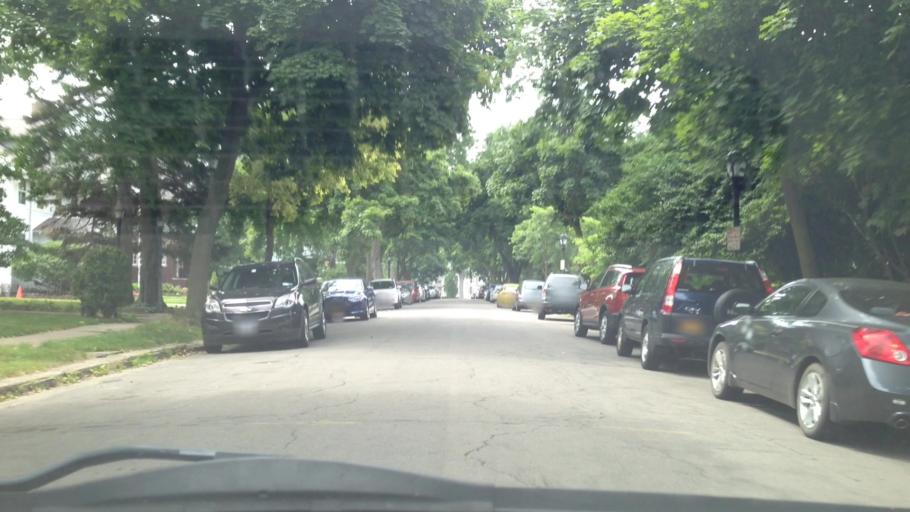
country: US
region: New York
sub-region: Erie County
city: Kenmore
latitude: 42.9354
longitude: -78.8479
